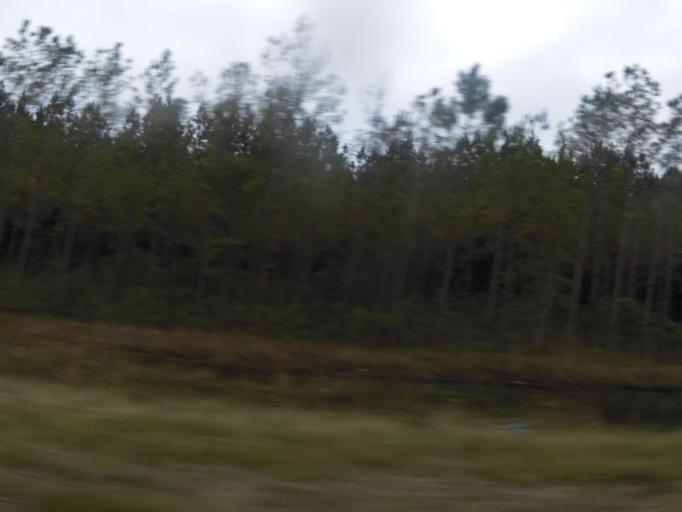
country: US
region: Georgia
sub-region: Charlton County
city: Folkston
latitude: 30.8912
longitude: -82.0496
